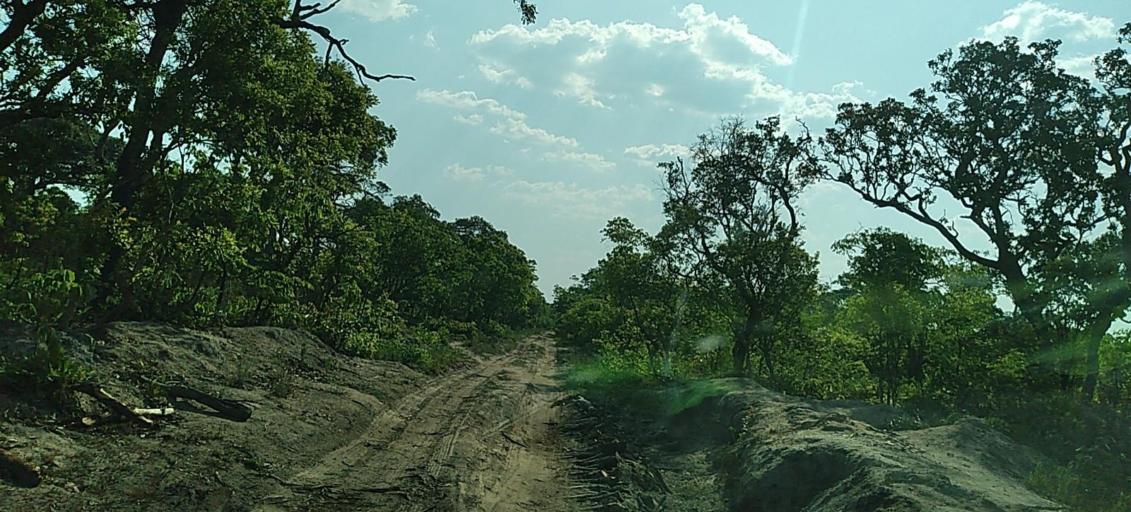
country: ZM
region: North-Western
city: Mwinilunga
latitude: -11.3078
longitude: 24.7885
